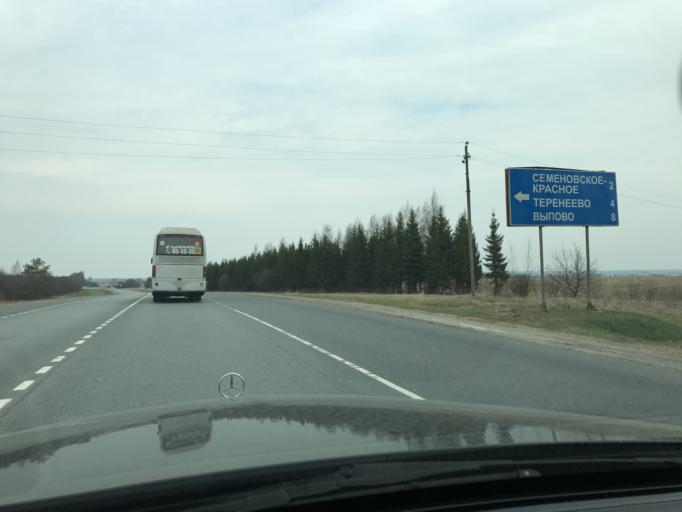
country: RU
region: Vladimir
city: Suzdal'
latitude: 56.3416
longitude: 40.4749
